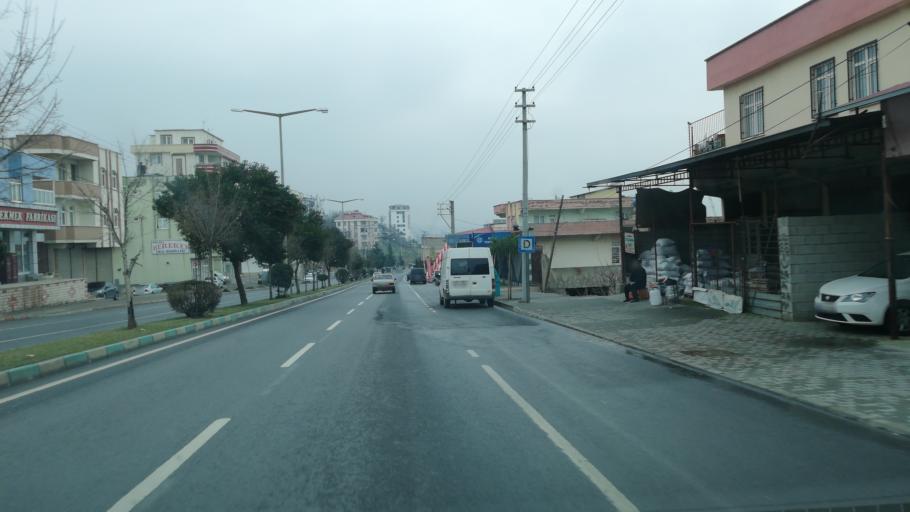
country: TR
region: Kahramanmaras
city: Kahramanmaras
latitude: 37.5823
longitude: 36.9532
